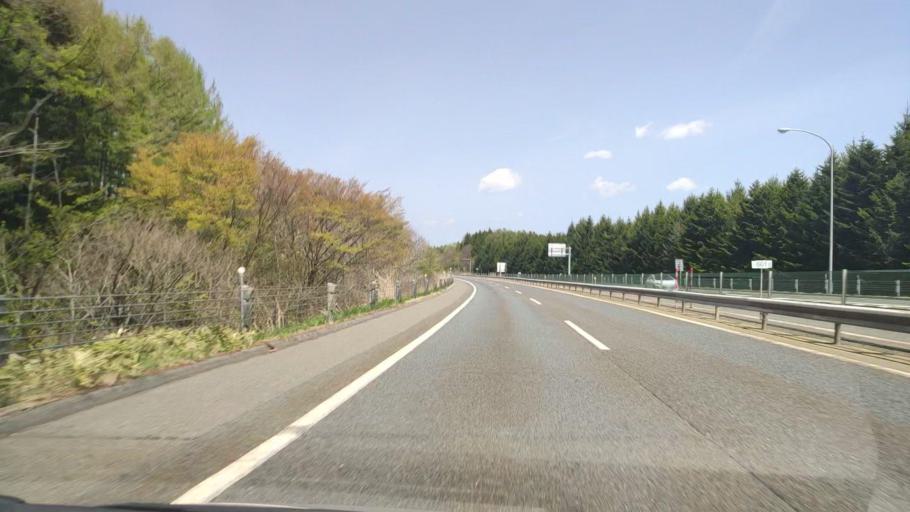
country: JP
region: Iwate
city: Ichinohe
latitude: 40.2550
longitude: 141.4027
